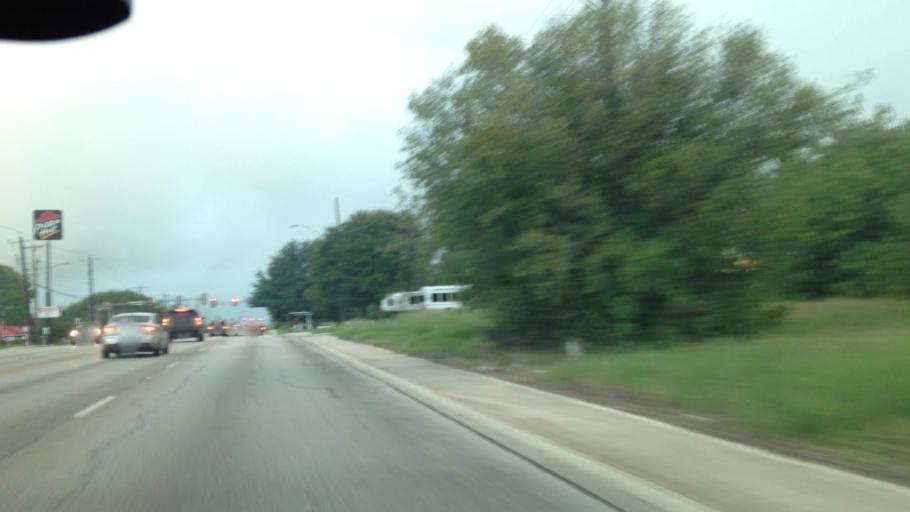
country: US
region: Texas
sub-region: Bexar County
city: Live Oak
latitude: 29.5746
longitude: -98.3773
